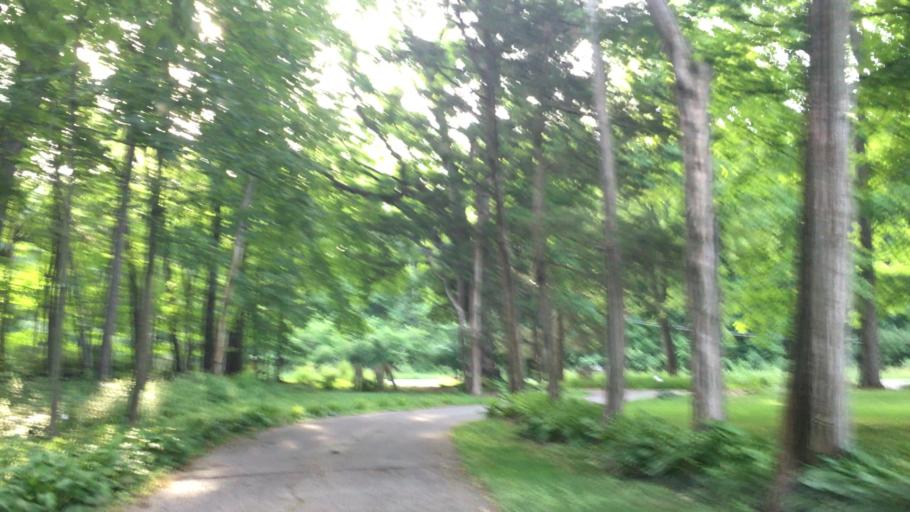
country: US
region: Iowa
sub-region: Johnson County
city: Iowa City
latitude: 41.6890
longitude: -91.5388
